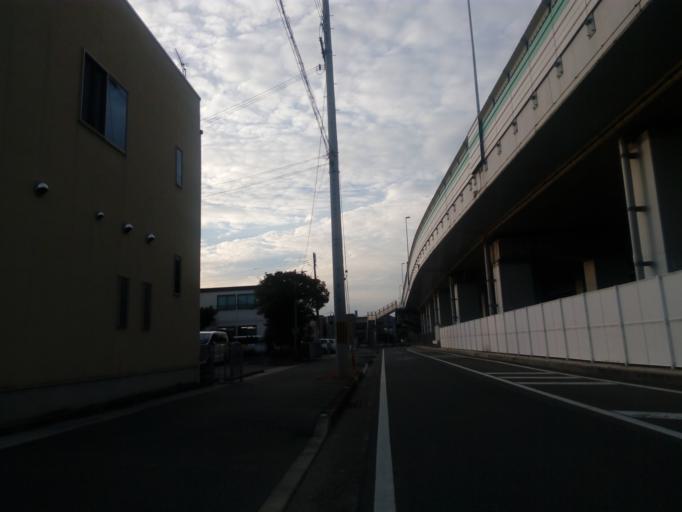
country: JP
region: Hyogo
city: Himeji
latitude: 34.8126
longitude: 134.6797
